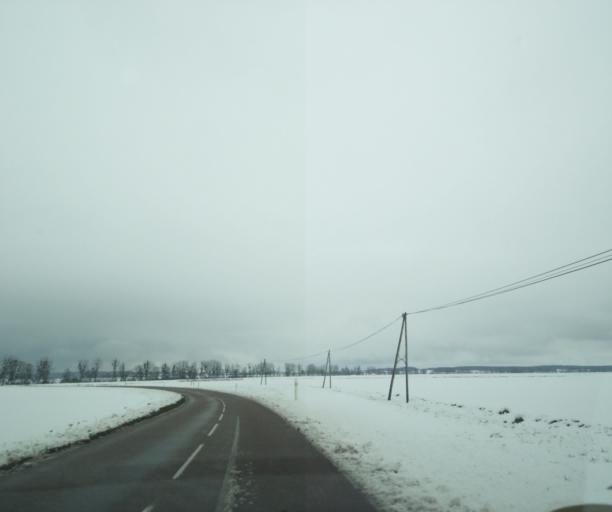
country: FR
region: Champagne-Ardenne
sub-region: Departement de la Haute-Marne
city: Montier-en-Der
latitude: 48.4475
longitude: 4.7854
